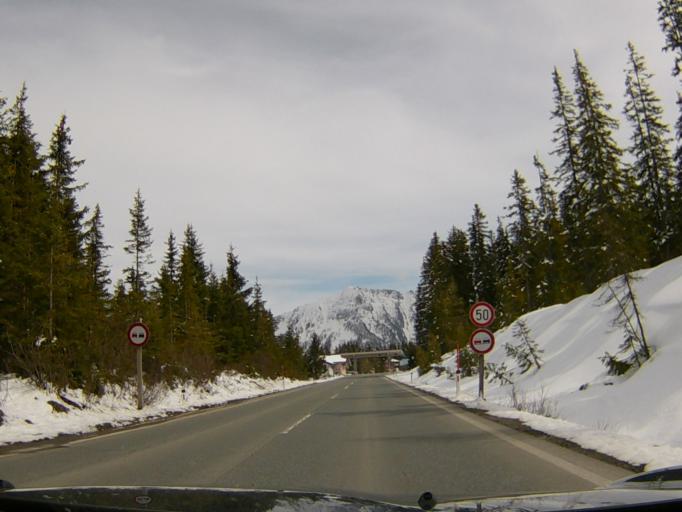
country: AT
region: Salzburg
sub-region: Politischer Bezirk Zell am See
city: Krimml
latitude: 47.2380
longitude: 12.1561
